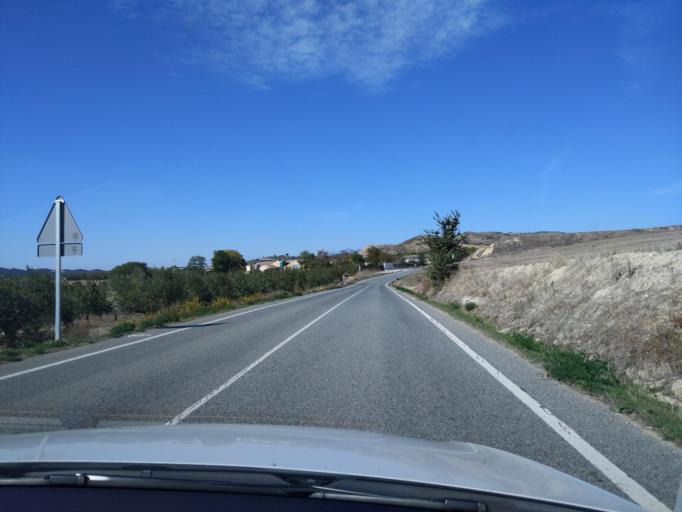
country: ES
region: Navarre
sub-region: Provincia de Navarra
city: Arroniz
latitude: 42.5681
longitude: -2.0732
